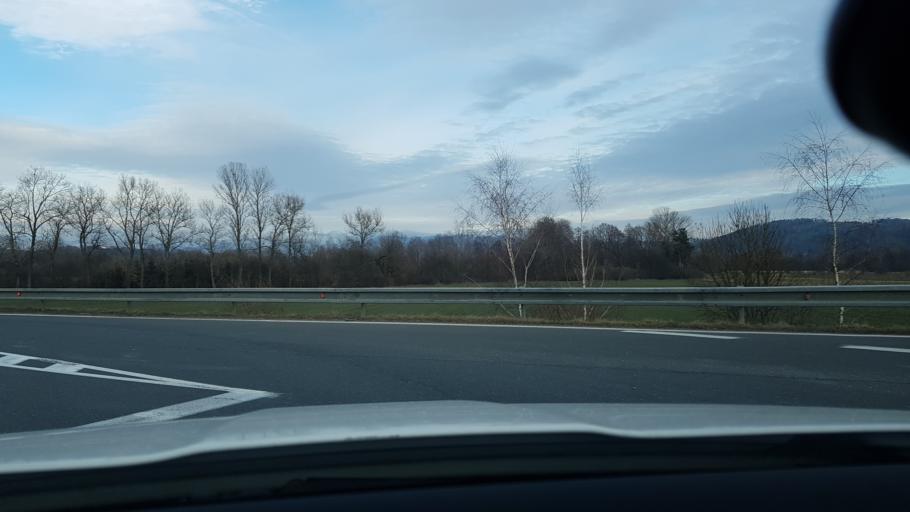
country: CZ
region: Olomoucky
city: Postrelmov
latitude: 49.9169
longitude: 16.9174
